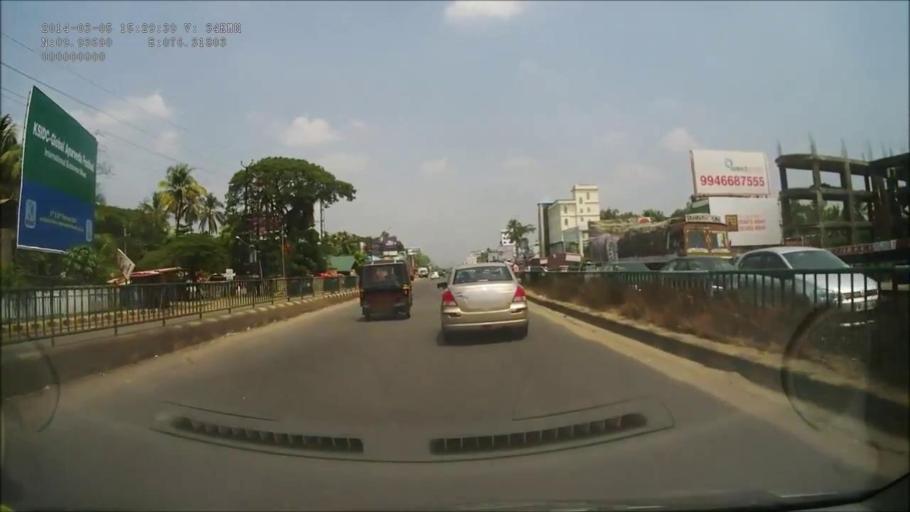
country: IN
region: Kerala
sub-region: Ernakulam
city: Cochin
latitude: 9.9379
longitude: 76.3179
